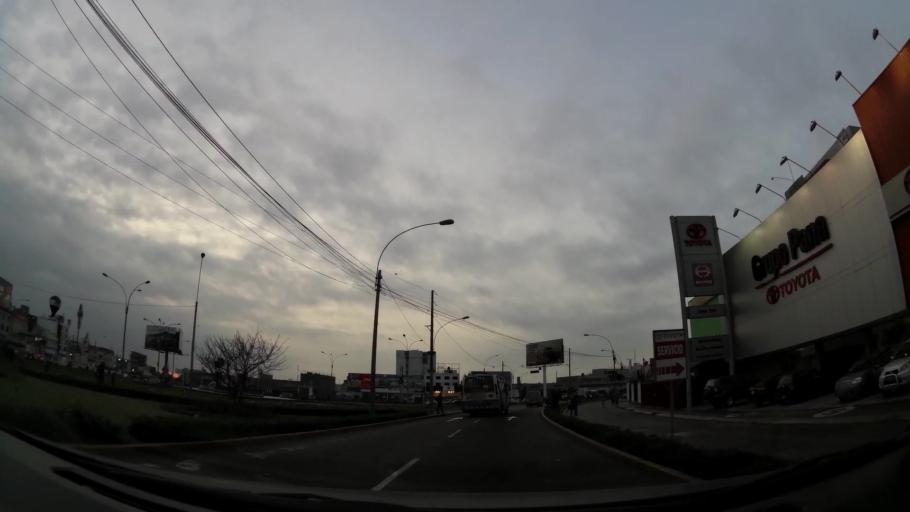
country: PE
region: Callao
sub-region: Callao
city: Callao
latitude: -12.0744
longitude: -77.0987
